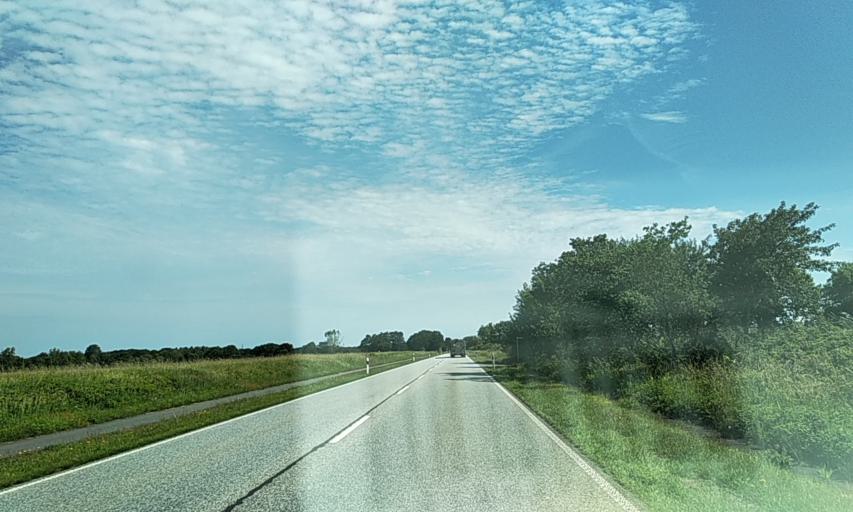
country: DE
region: Schleswig-Holstein
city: Jagel
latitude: 54.4654
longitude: 9.5410
